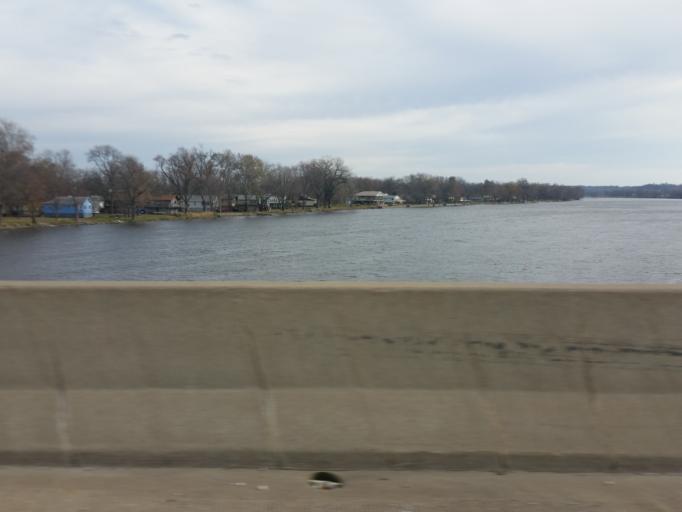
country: US
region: Illinois
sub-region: Rock Island County
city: Coal Valley
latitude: 41.4609
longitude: -90.4950
